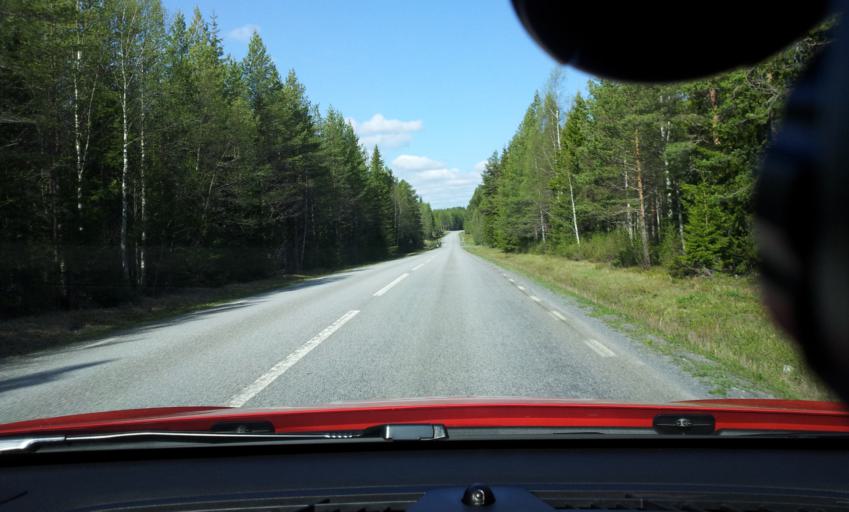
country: SE
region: Jaemtland
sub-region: Krokoms Kommun
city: Krokom
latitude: 63.1283
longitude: 14.2298
